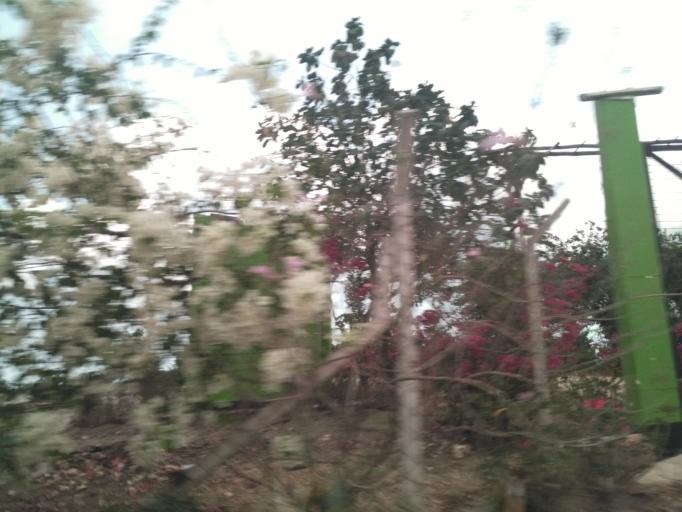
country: TZ
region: Dar es Salaam
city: Dar es Salaam
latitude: -6.8555
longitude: 39.3611
